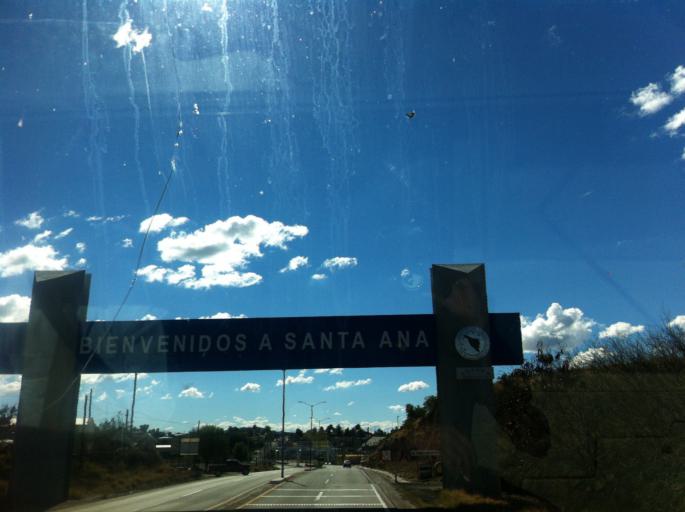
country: MX
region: Sonora
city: Santa Ana
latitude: 30.5486
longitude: -111.1115
